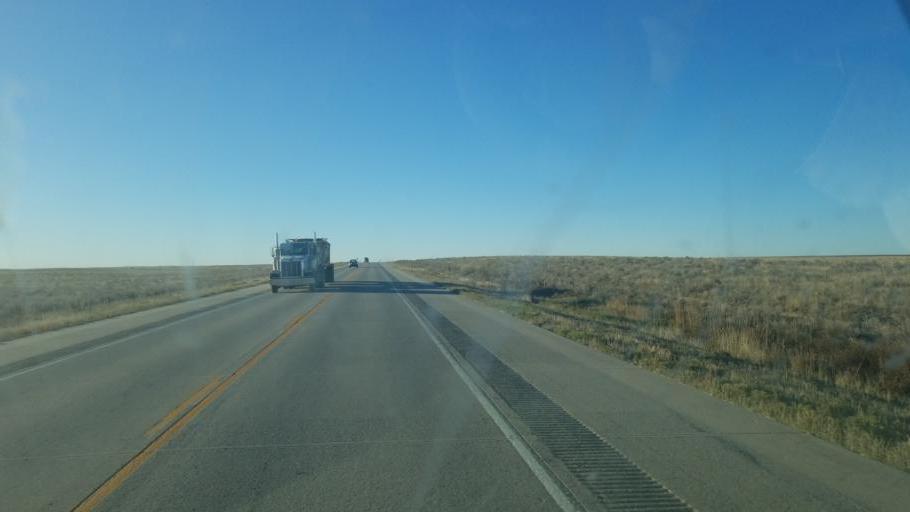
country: US
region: Colorado
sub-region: Kiowa County
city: Eads
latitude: 38.5838
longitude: -102.7861
